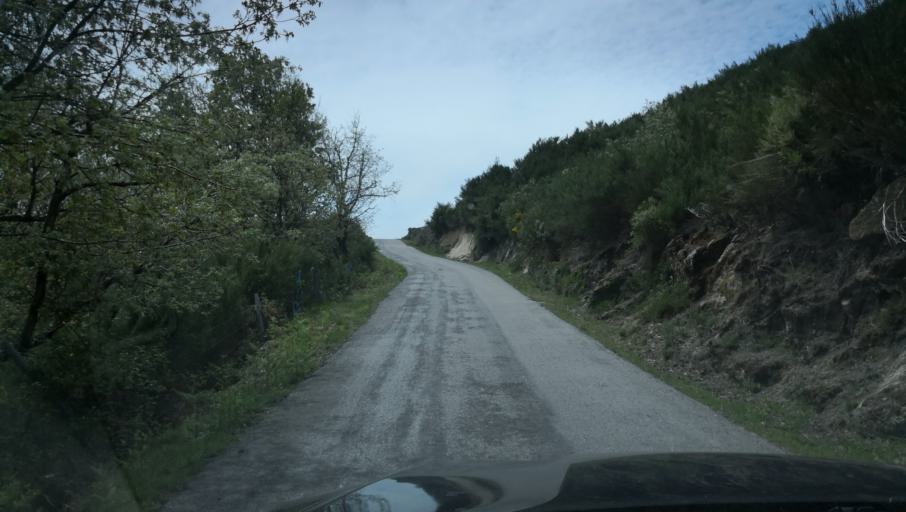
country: PT
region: Vila Real
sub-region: Vila Real
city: Vila Real
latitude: 41.3009
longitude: -7.8117
